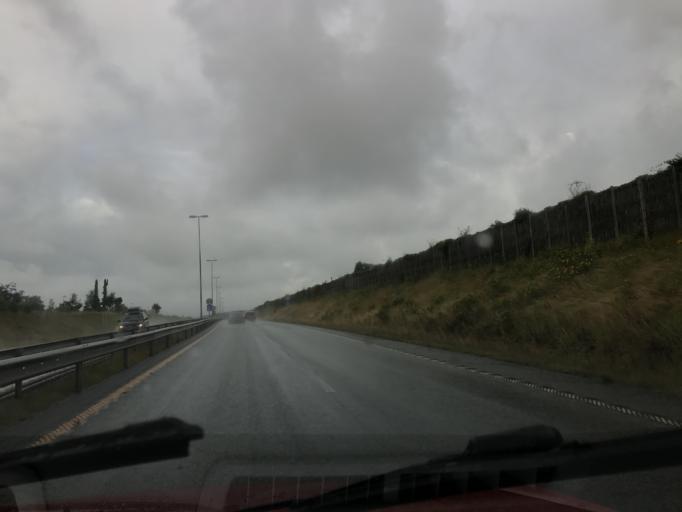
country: NO
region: Aust-Agder
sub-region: Grimstad
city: Grimstad
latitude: 58.3407
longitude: 8.5643
